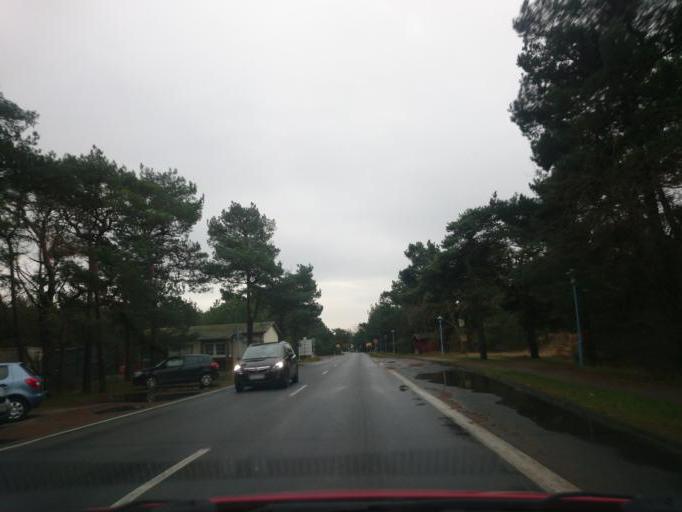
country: DE
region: Mecklenburg-Vorpommern
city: Altenkirchen
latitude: 54.6135
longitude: 13.3792
